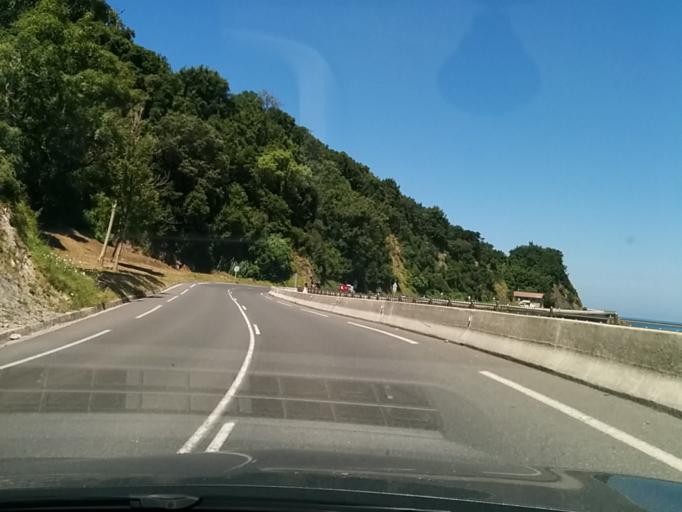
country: ES
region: Basque Country
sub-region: Provincia de Guipuzcoa
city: Getaria
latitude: 43.2948
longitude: -2.1914
